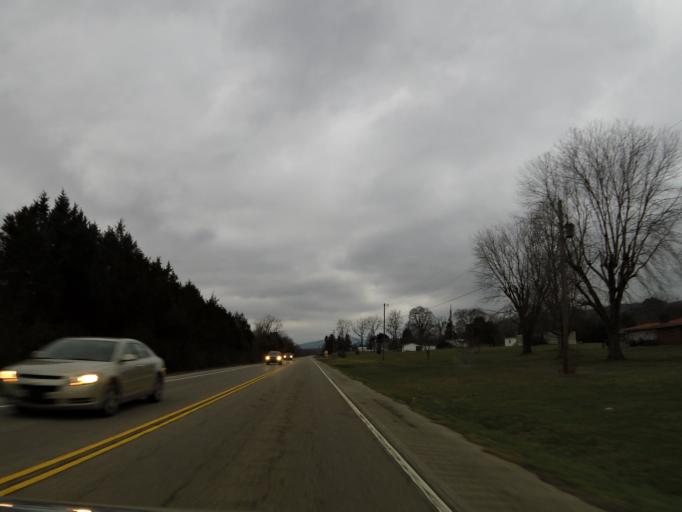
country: US
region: Tennessee
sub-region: Grainger County
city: Rutledge
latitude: 36.2390
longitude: -83.6127
